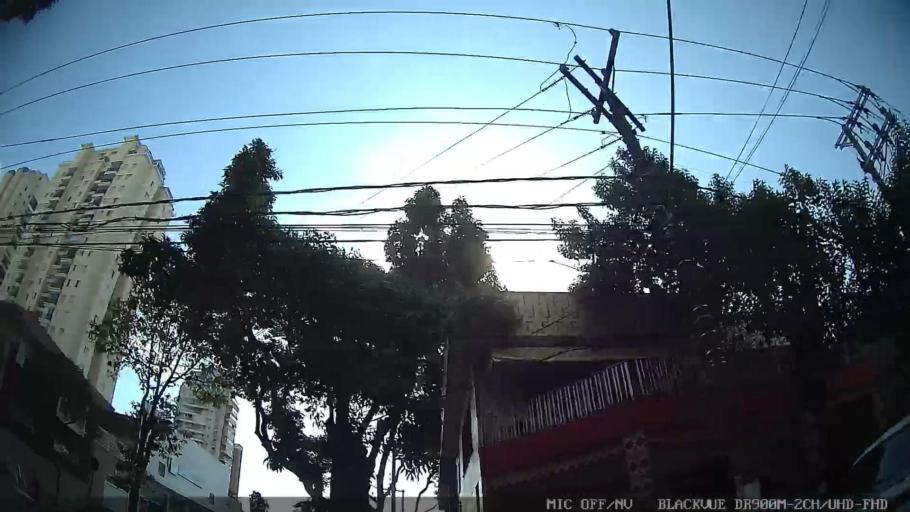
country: BR
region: Sao Paulo
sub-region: Sao Paulo
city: Sao Paulo
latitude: -23.5756
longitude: -46.6052
